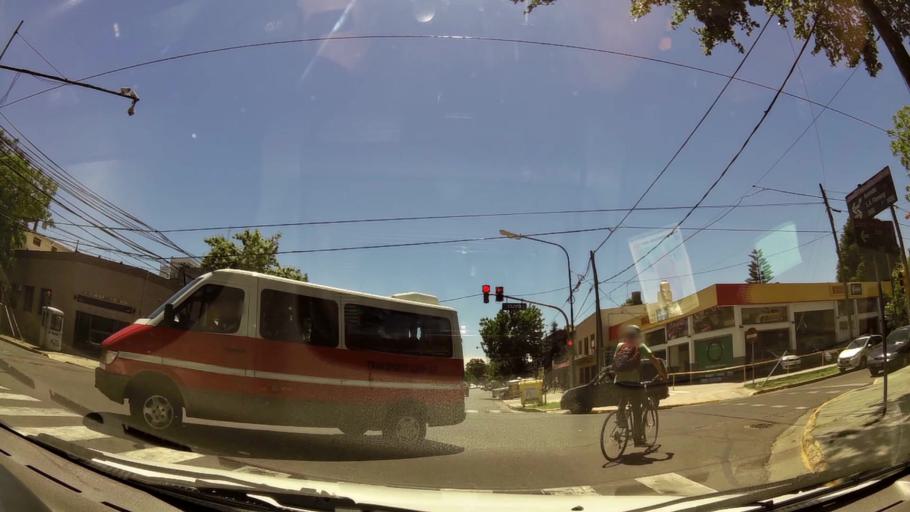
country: AR
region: Buenos Aires
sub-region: Partido de San Isidro
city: San Isidro
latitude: -34.4934
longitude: -58.5226
